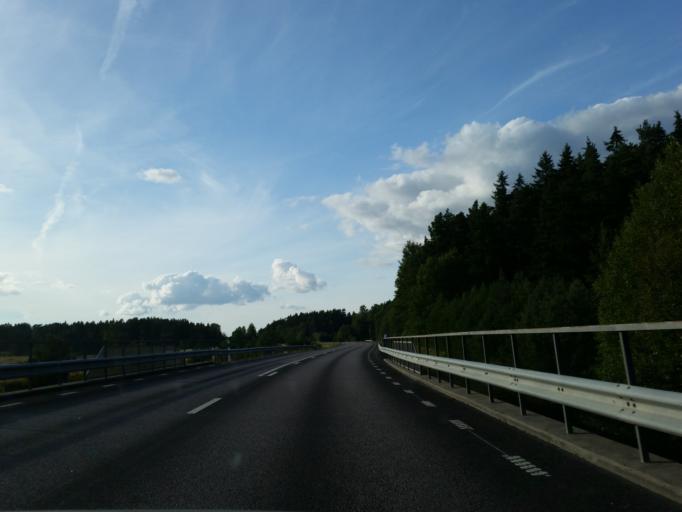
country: SE
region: Soedermanland
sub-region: Gnesta Kommun
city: Gnesta
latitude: 59.0405
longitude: 17.2946
